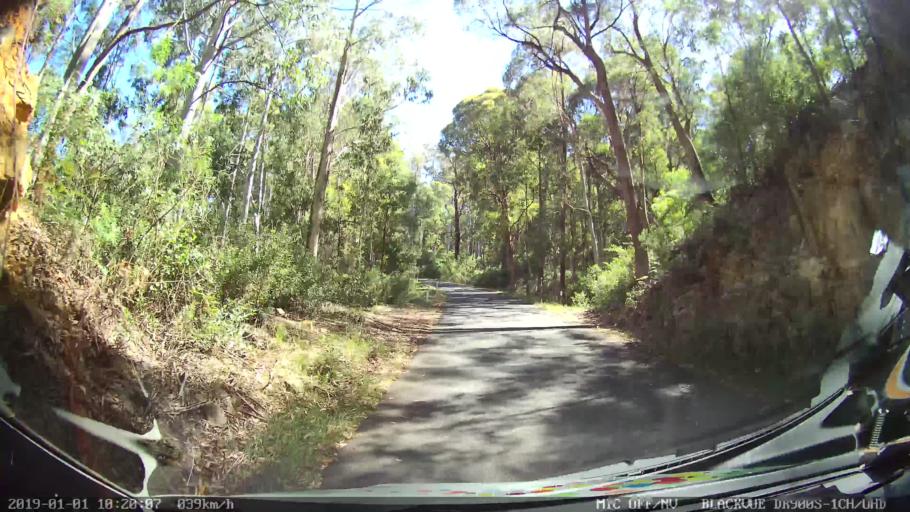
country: AU
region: New South Wales
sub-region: Snowy River
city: Jindabyne
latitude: -36.0803
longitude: 148.1872
